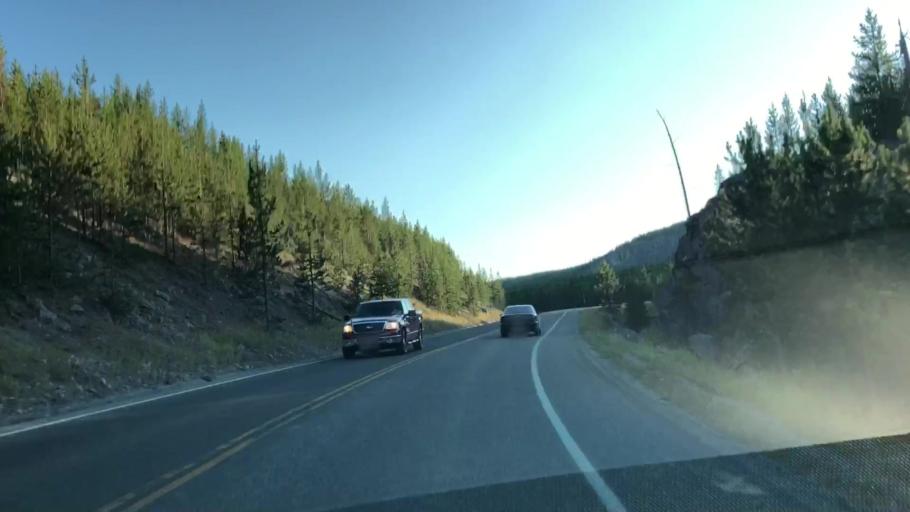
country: US
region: Montana
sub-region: Gallatin County
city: West Yellowstone
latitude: 44.6304
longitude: -110.8547
